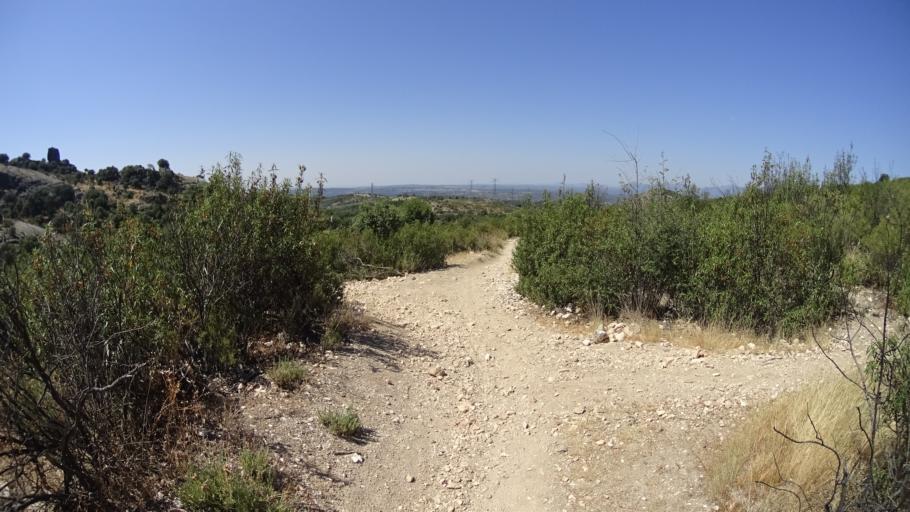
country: ES
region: Madrid
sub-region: Provincia de Madrid
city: Moralzarzal
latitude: 40.6371
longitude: -3.9514
